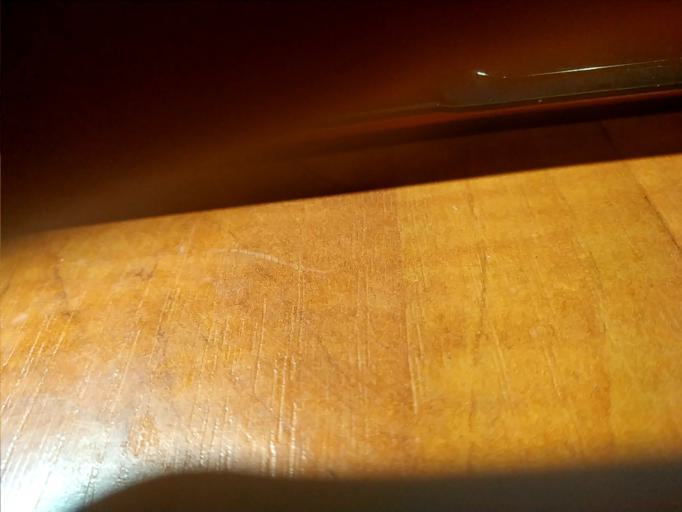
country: RU
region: Tverskaya
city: Ves'yegonsk
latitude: 58.7189
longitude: 37.5439
